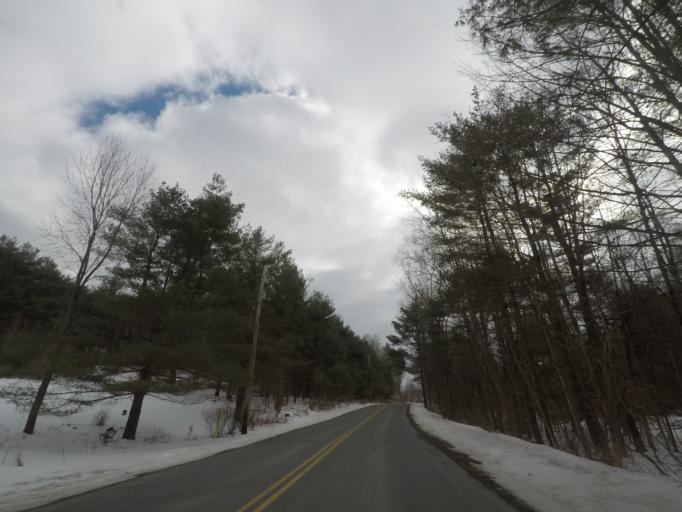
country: US
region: New York
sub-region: Rensselaer County
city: Hoosick Falls
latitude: 42.8899
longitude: -73.4194
